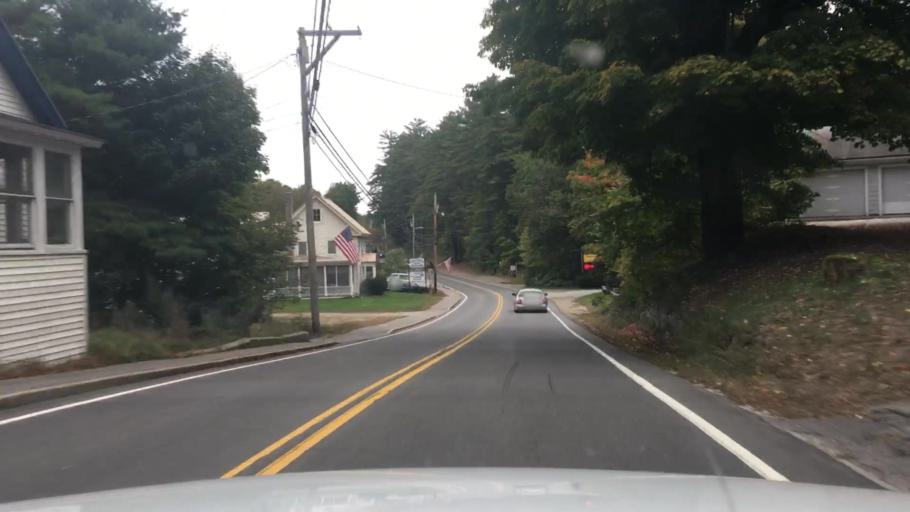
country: US
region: New Hampshire
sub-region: Strafford County
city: New Durham
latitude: 43.4691
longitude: -71.2318
